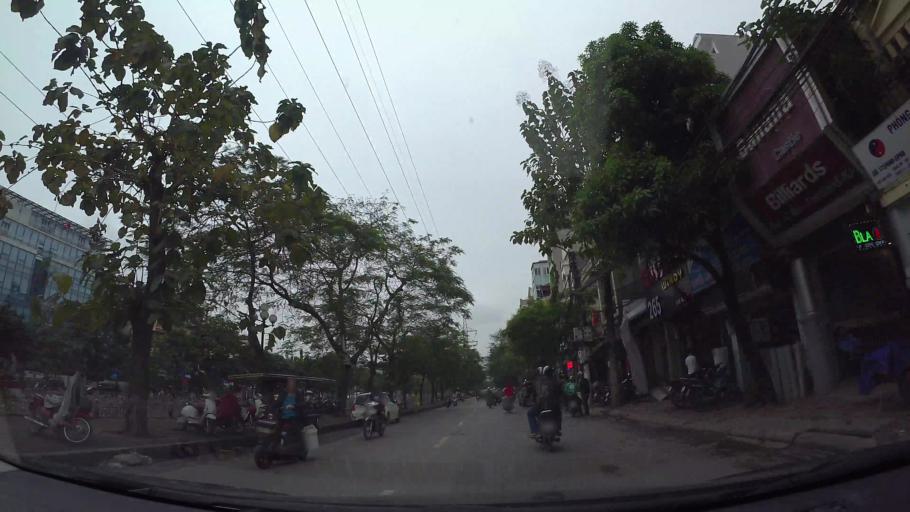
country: VN
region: Ha Noi
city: Hai BaTrung
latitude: 21.0043
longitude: 105.8616
